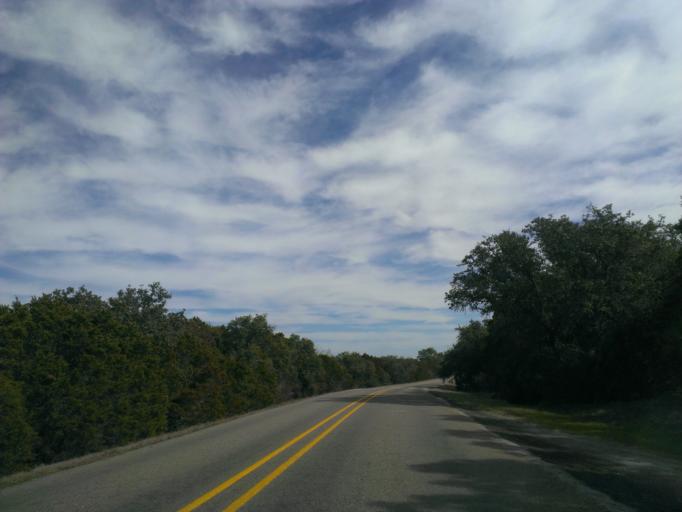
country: US
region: Texas
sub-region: Llano County
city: Buchanan Dam
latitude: 30.6967
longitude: -98.3604
